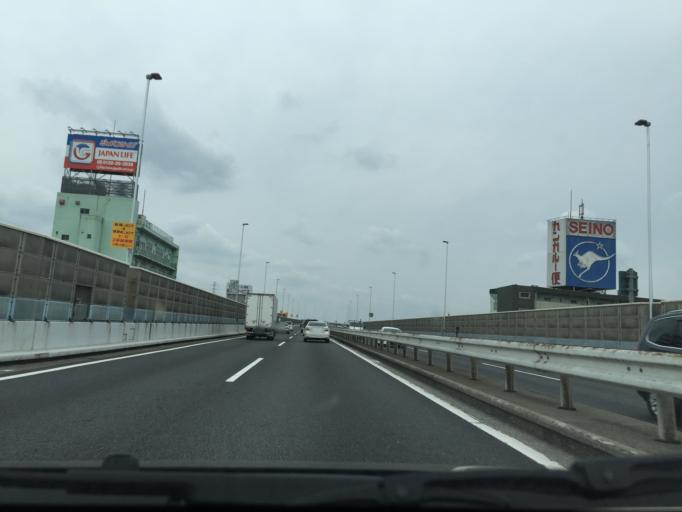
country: JP
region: Saitama
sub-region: Kawaguchi-shi
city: Hatogaya-honcho
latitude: 35.8011
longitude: 139.7607
